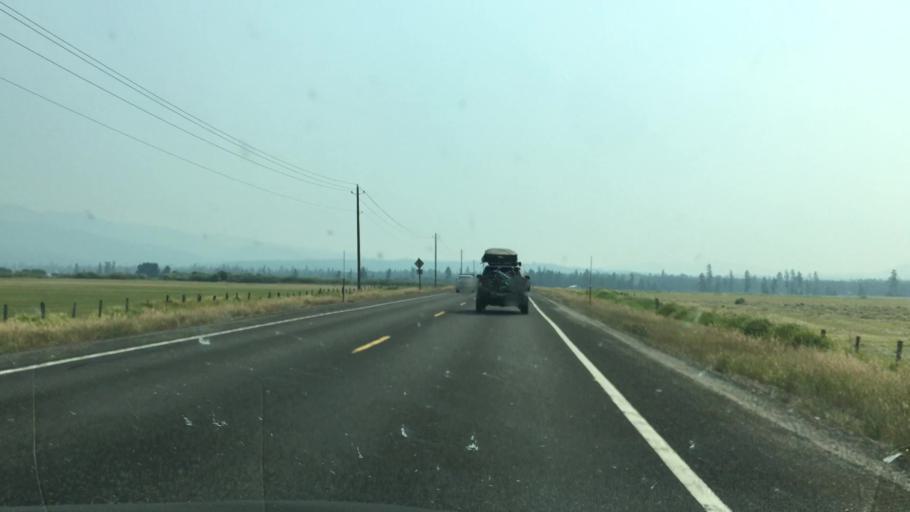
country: US
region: Idaho
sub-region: Valley County
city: Cascade
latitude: 44.4226
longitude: -115.9996
